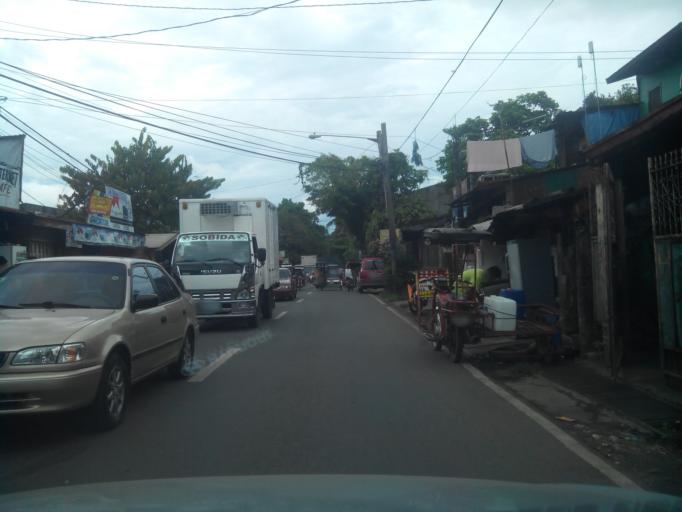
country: PH
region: Calabarzon
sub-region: Province of Rizal
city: Teresa
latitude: 14.5916
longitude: 121.1791
